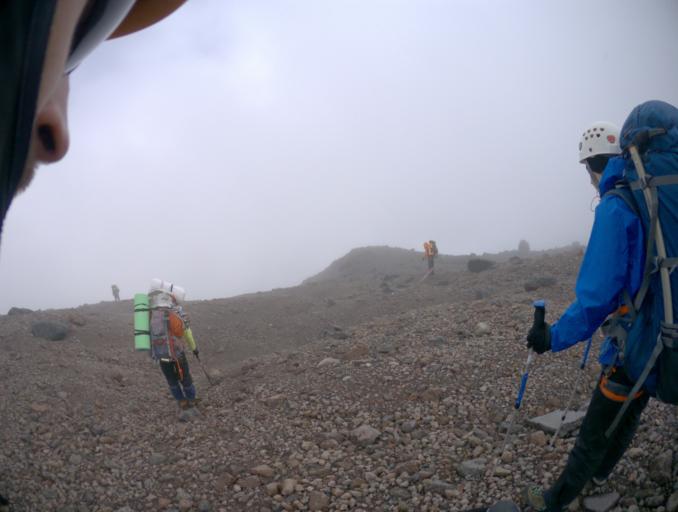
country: RU
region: Kabardino-Balkariya
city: Terskol
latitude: 43.3803
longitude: 42.4094
